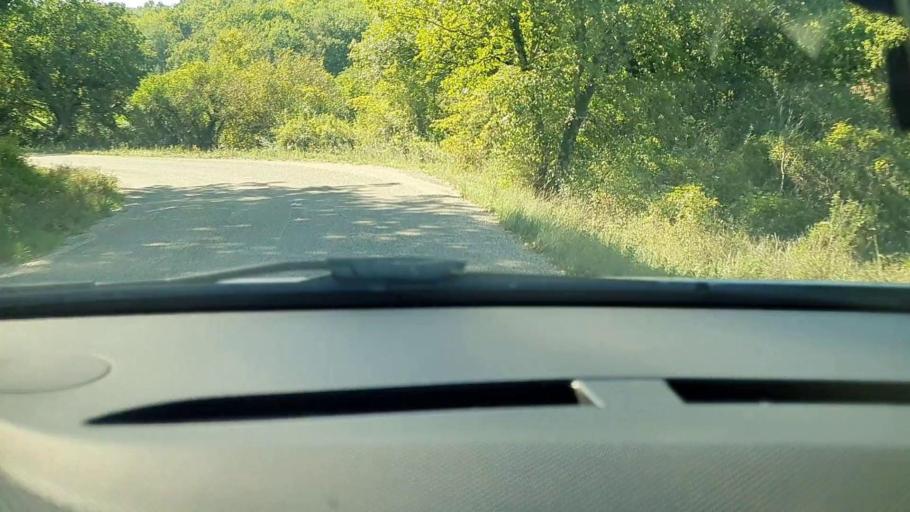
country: FR
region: Languedoc-Roussillon
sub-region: Departement du Gard
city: Saint-Ambroix
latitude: 44.2253
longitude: 4.2842
